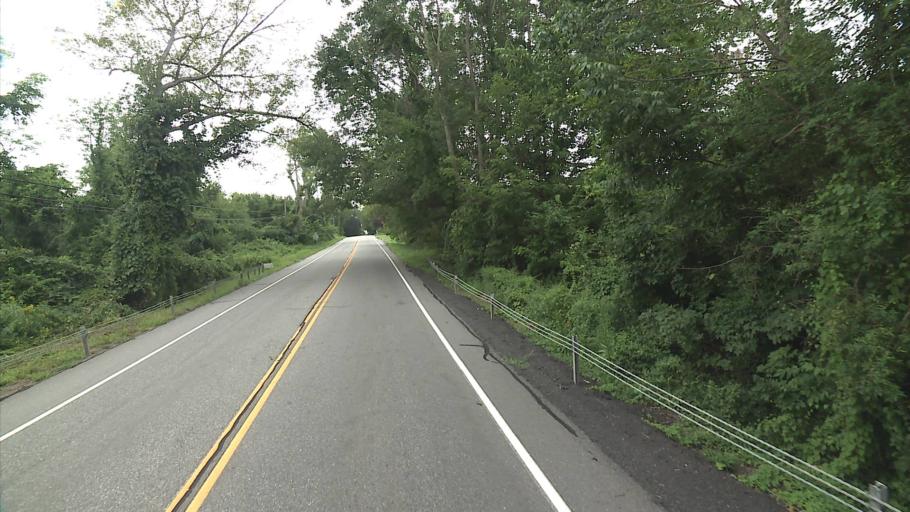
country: US
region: Connecticut
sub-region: Tolland County
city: Storrs
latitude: 41.8697
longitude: -72.2078
